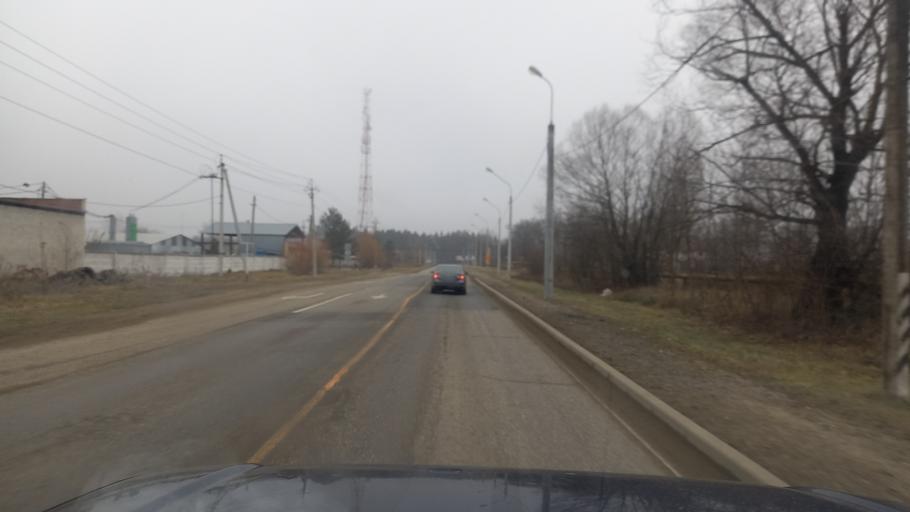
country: RU
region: Krasnodarskiy
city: Apsheronsk
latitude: 44.4382
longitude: 39.7583
